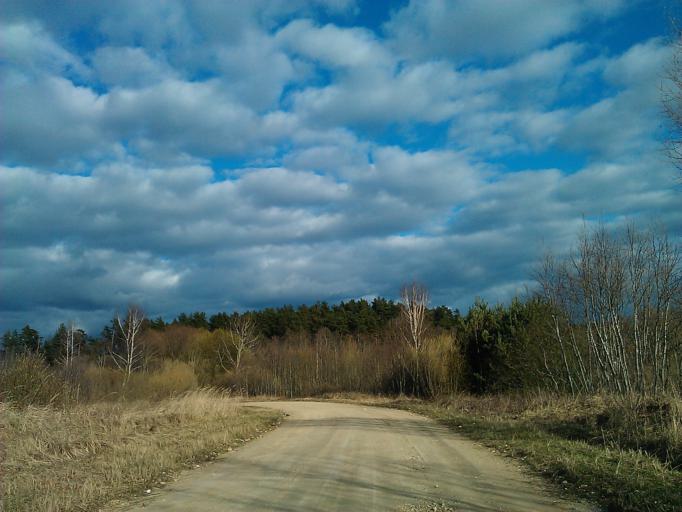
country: LV
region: Adazi
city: Adazi
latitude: 57.0616
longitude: 24.3444
